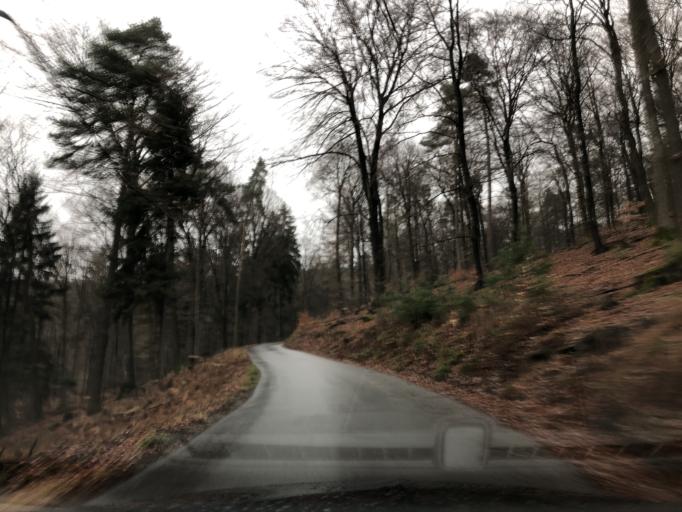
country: DE
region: Baden-Wuerttemberg
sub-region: Karlsruhe Region
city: Dossenheim
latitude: 49.4504
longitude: 8.7071
